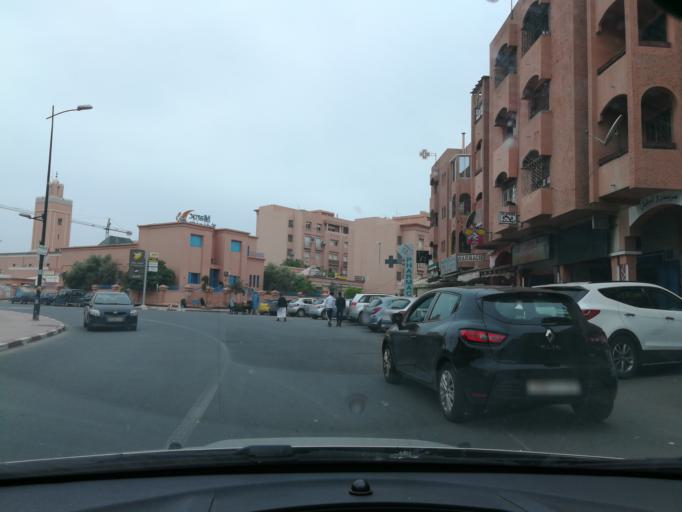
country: MA
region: Marrakech-Tensift-Al Haouz
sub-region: Marrakech
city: Marrakesh
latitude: 31.6581
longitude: -8.0030
